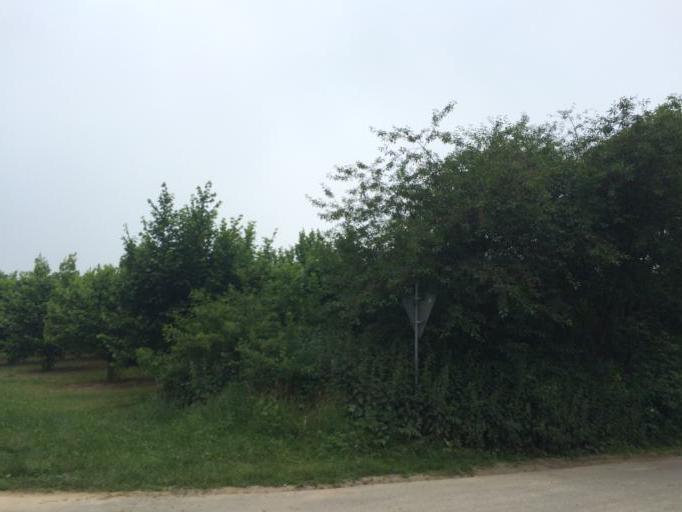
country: PL
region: Lublin Voivodeship
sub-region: Powiat pulawski
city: Markuszow
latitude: 51.3593
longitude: 22.2683
